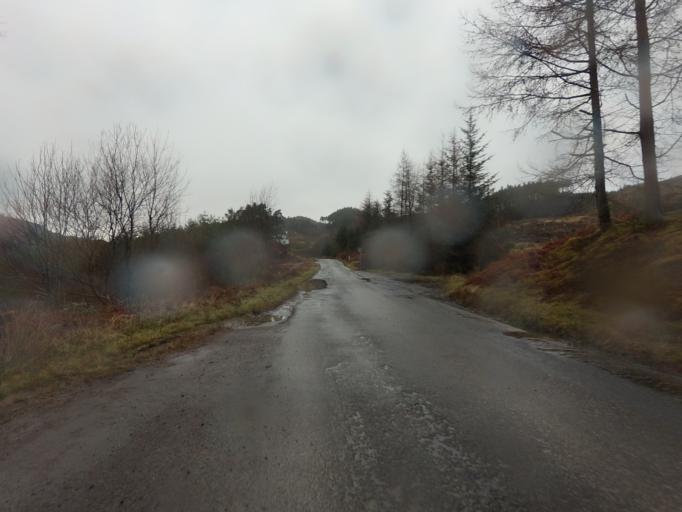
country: GB
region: Scotland
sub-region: West Dunbartonshire
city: Balloch
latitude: 56.2348
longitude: -4.5612
